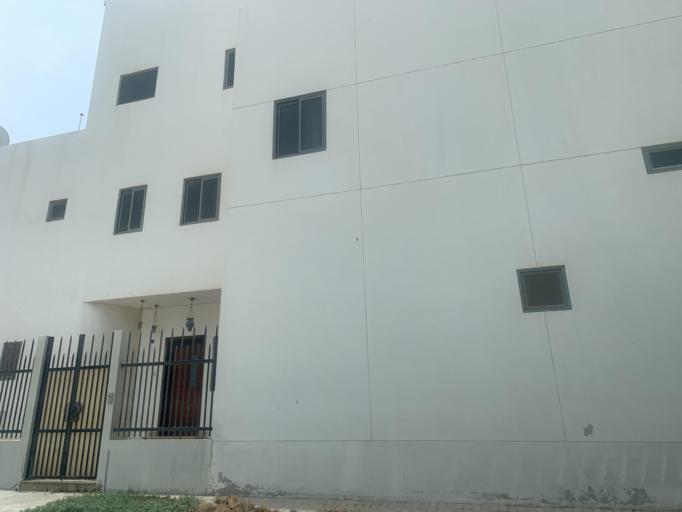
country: BH
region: Muharraq
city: Al Hadd
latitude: 26.2938
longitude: 50.6697
